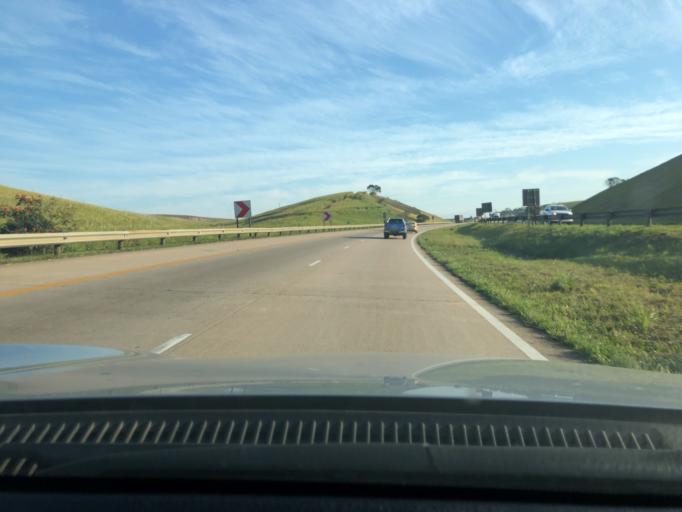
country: ZA
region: KwaZulu-Natal
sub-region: iLembe District Municipality
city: Stanger
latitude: -29.3876
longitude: 31.2973
